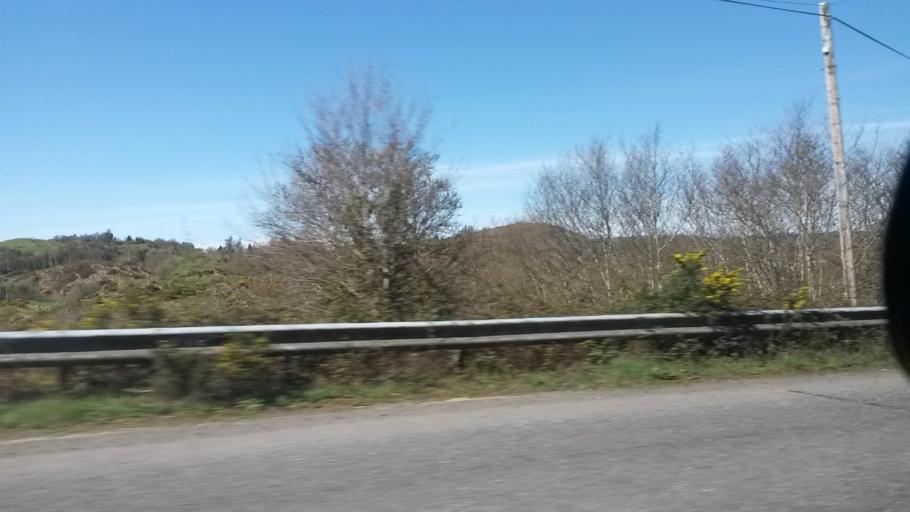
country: IE
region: Munster
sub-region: County Cork
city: Millstreet
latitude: 51.9274
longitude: -9.1212
